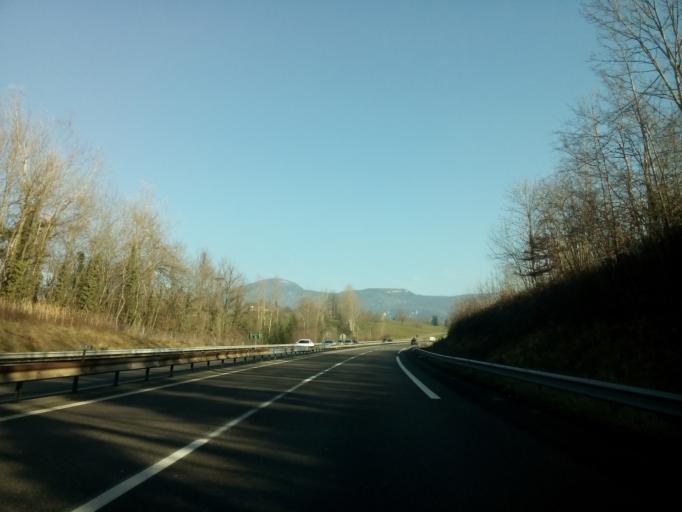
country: FR
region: Rhone-Alpes
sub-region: Departement de la Savoie
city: Novalaise
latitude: 45.5605
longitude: 5.7609
